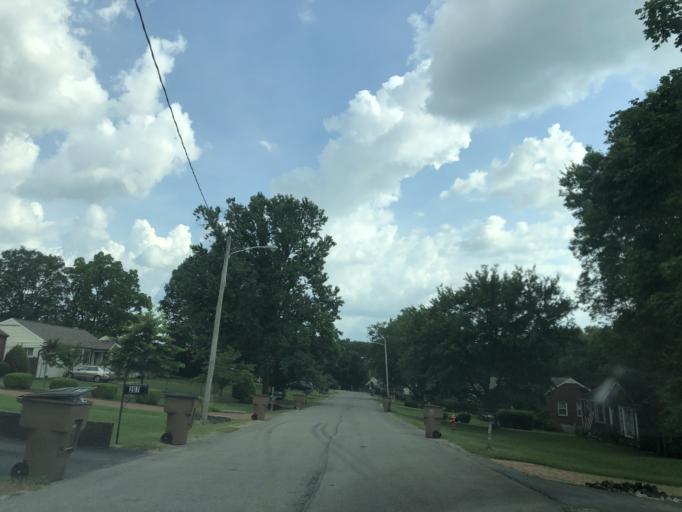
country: US
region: Tennessee
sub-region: Davidson County
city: Lakewood
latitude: 36.1670
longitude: -86.6771
